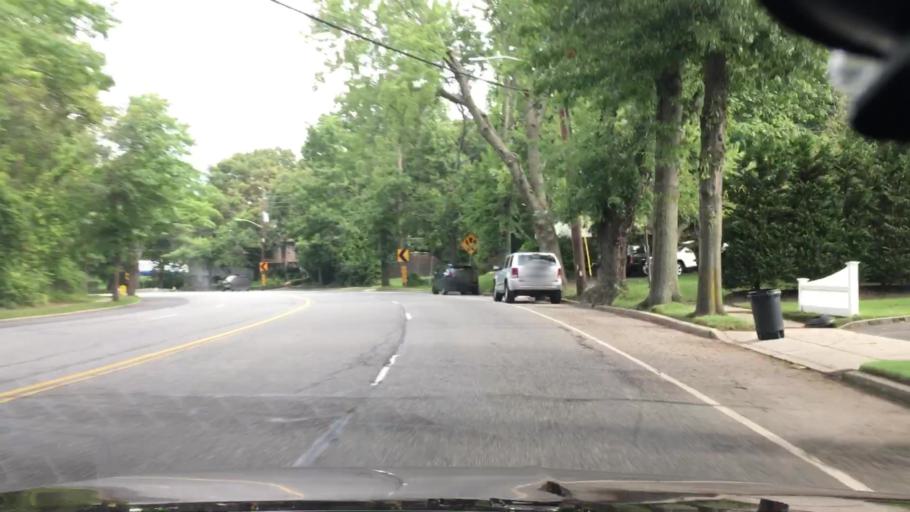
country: US
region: New York
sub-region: Nassau County
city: Old Bethpage
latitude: 40.7801
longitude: -73.4447
